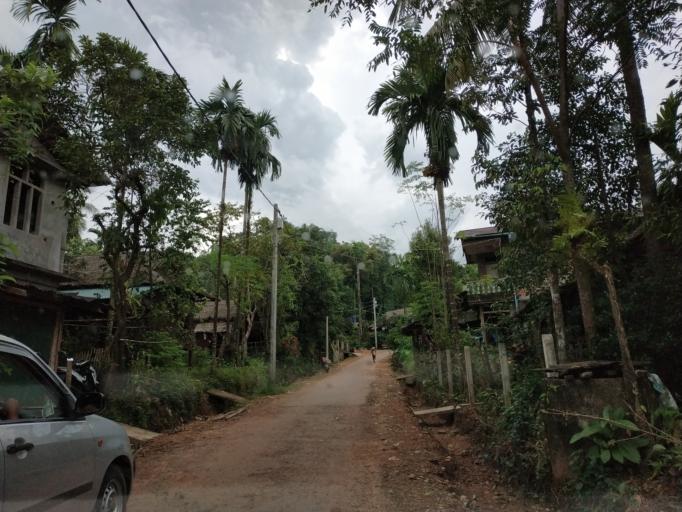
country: MM
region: Tanintharyi
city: Dawei
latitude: 13.8622
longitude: 98.2655
